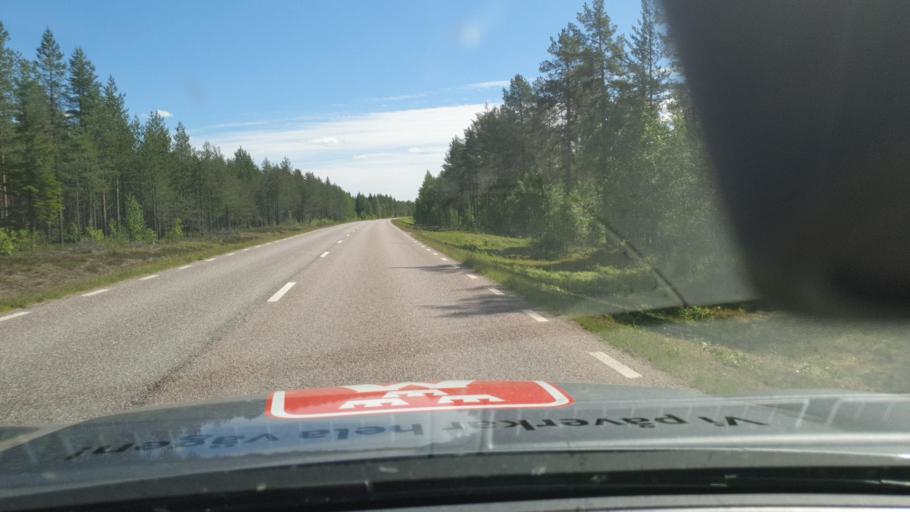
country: FI
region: Lapland
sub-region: Tunturi-Lappi
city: Kolari
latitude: 67.0121
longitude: 23.7393
